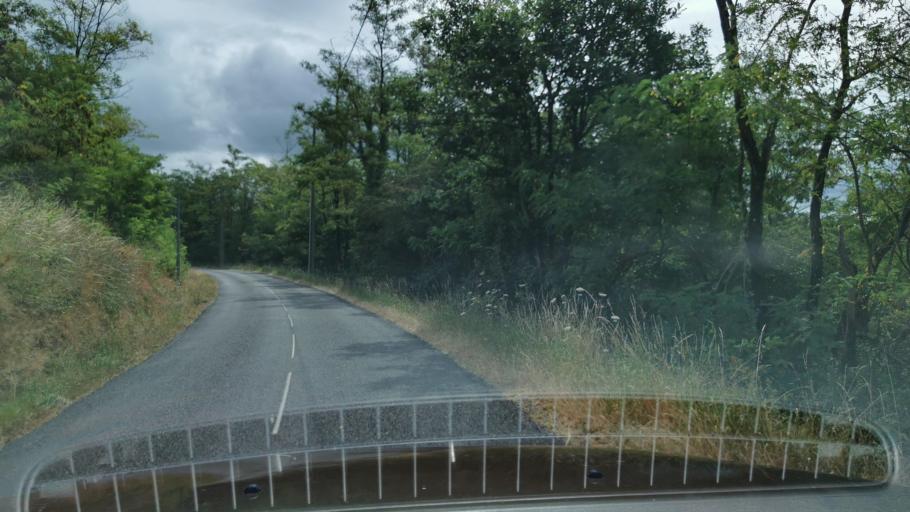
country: FR
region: Bourgogne
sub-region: Departement de Saone-et-Loire
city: Montcenis
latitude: 46.7931
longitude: 4.3753
